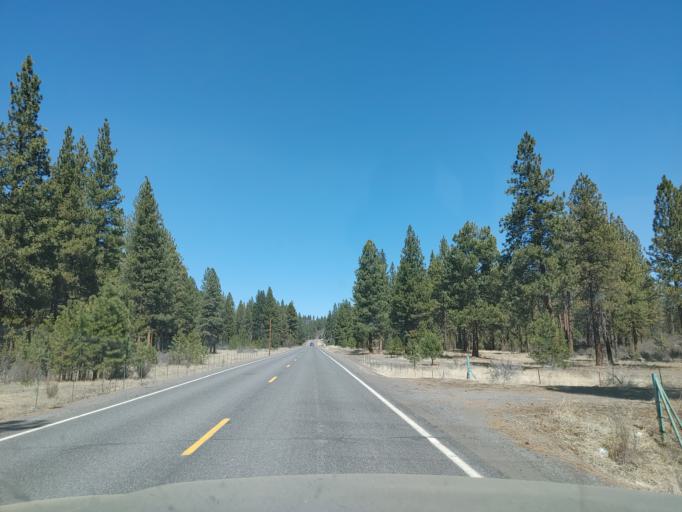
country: US
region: Oregon
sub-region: Klamath County
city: Klamath Falls
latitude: 42.5517
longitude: -121.8960
